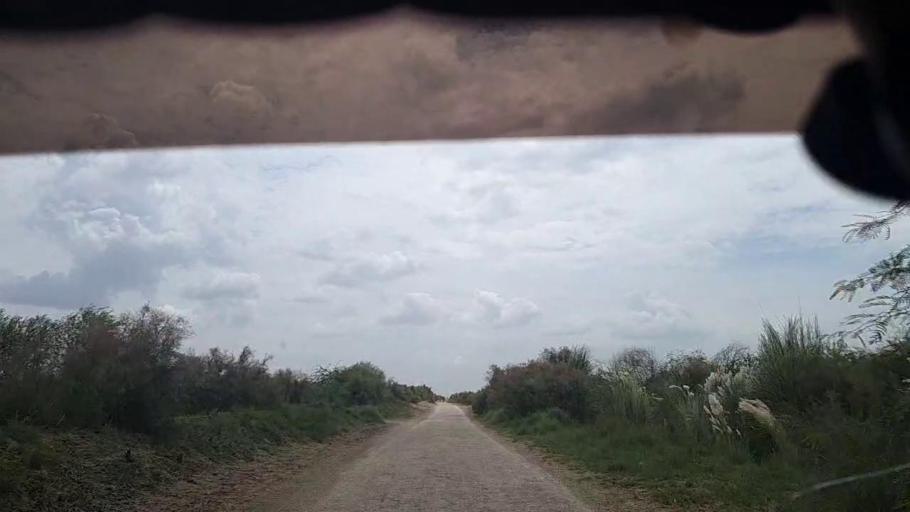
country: PK
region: Sindh
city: Rustam jo Goth
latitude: 28.0344
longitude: 68.9375
